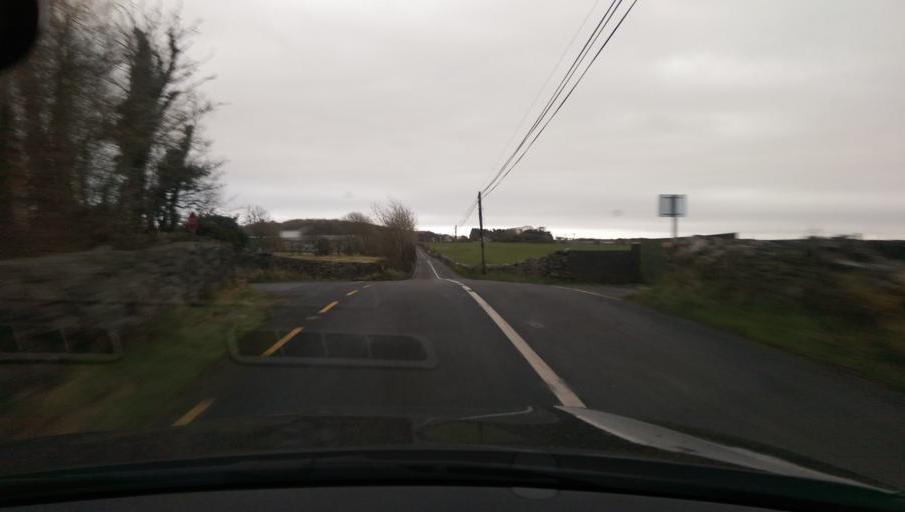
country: IE
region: Connaught
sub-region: County Galway
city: Athenry
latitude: 53.3107
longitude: -8.7969
